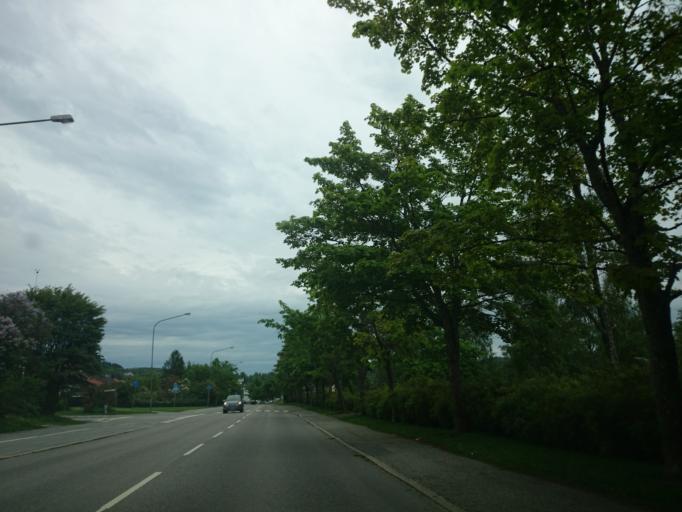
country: SE
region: Vaesternorrland
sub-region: Haernoesands Kommun
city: Haernoesand
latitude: 62.6298
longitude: 17.9528
